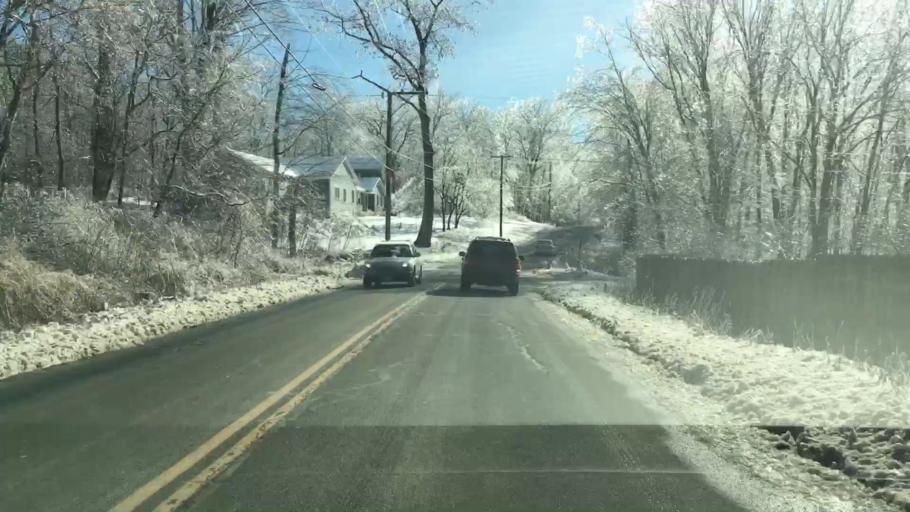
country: US
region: Connecticut
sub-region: Fairfield County
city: Newtown
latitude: 41.3806
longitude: -73.2587
